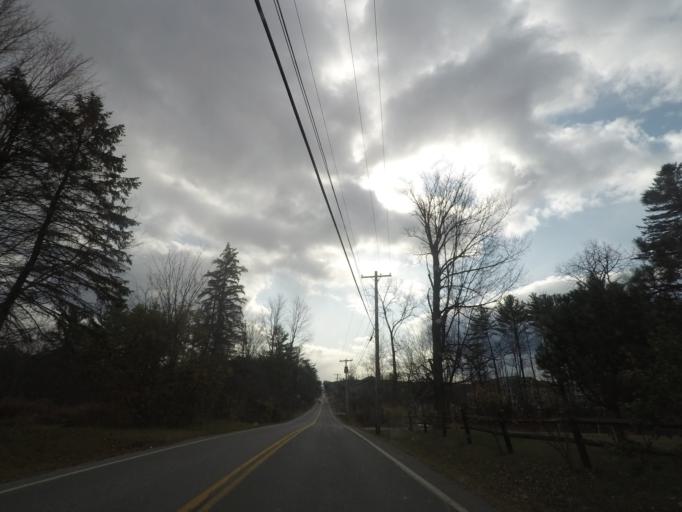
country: US
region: New York
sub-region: Saratoga County
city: Ballston Spa
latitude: 42.9749
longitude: -73.8315
